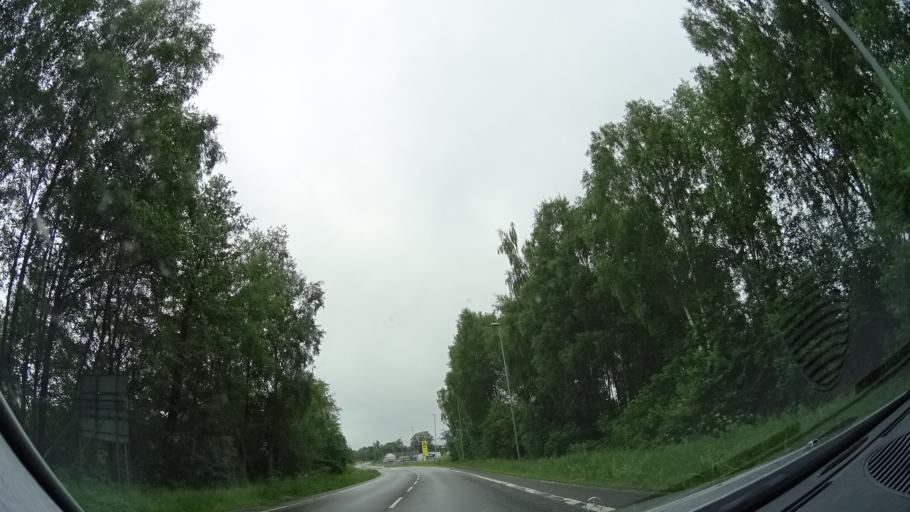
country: SE
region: Skane
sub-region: Hoors Kommun
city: Hoeoer
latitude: 55.9375
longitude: 13.5526
